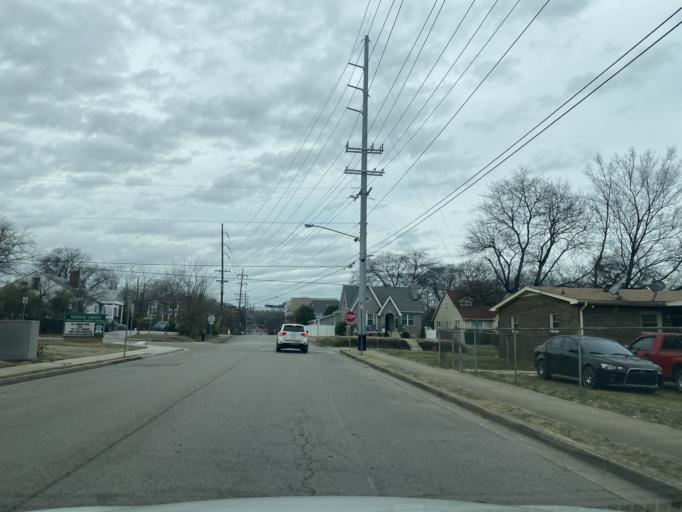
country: US
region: Tennessee
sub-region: Davidson County
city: Nashville
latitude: 36.1404
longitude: -86.7906
